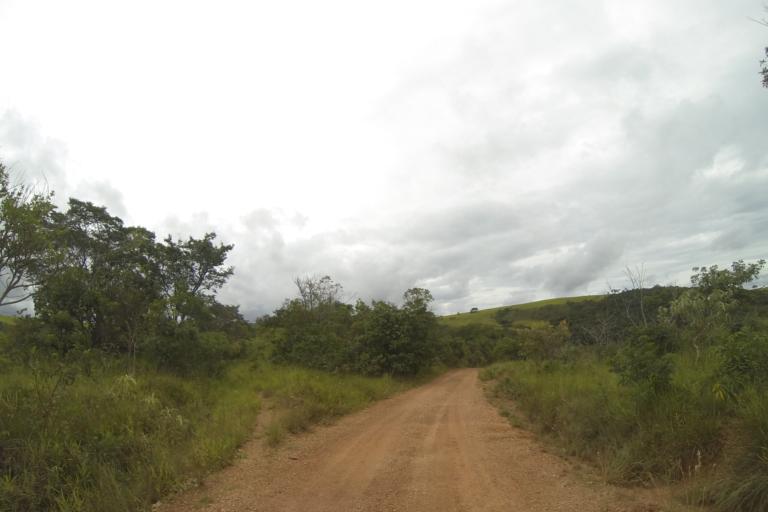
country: BR
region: Minas Gerais
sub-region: Ibia
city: Ibia
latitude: -19.7418
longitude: -46.5593
